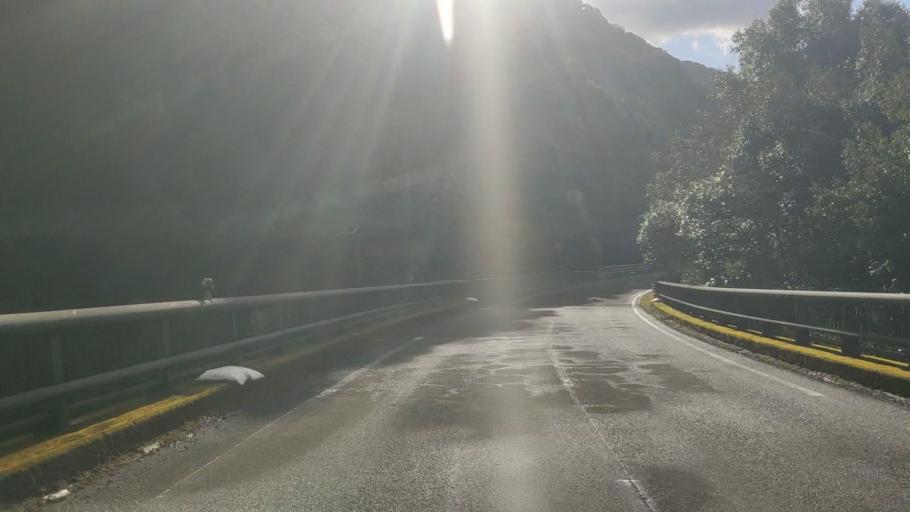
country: JP
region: Kumamoto
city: Hitoyoshi
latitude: 32.3792
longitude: 130.8378
